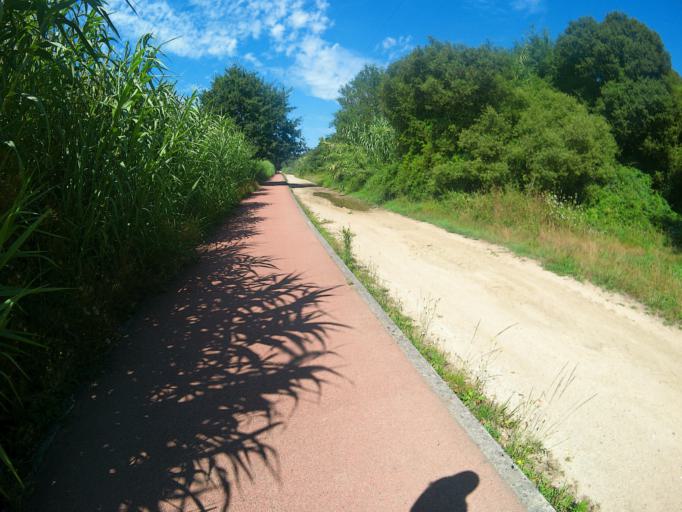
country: PT
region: Viana do Castelo
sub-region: Valenca
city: Valenca
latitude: 42.0055
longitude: -8.6562
